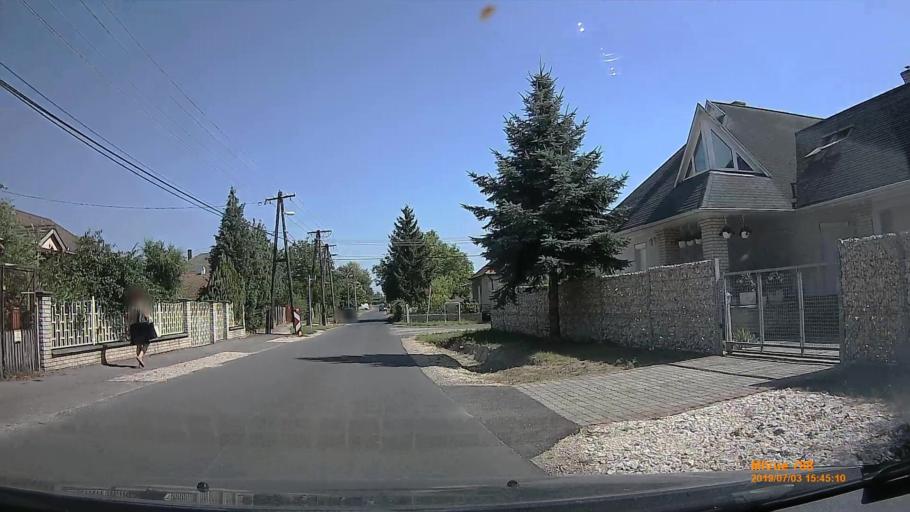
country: HU
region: Gyor-Moson-Sopron
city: Toltestava
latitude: 47.6943
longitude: 17.7593
